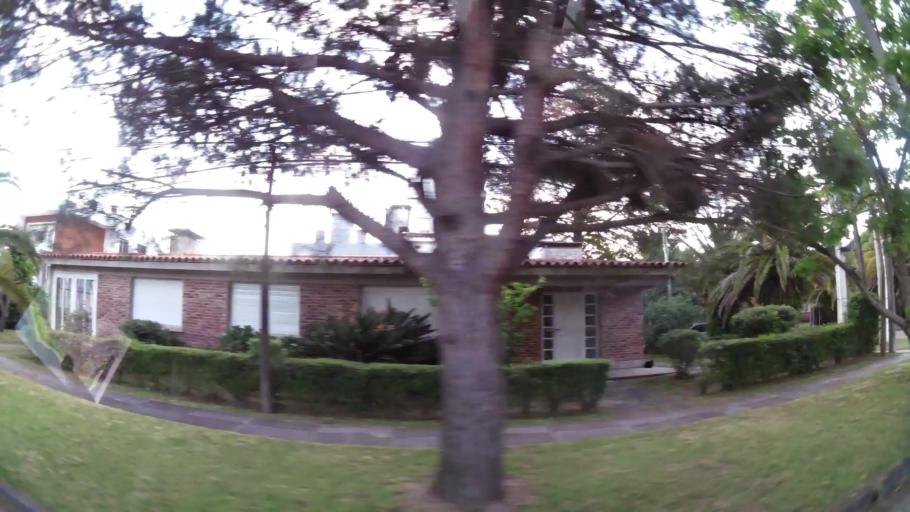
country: UY
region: Canelones
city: Atlantida
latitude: -34.7770
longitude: -55.7607
